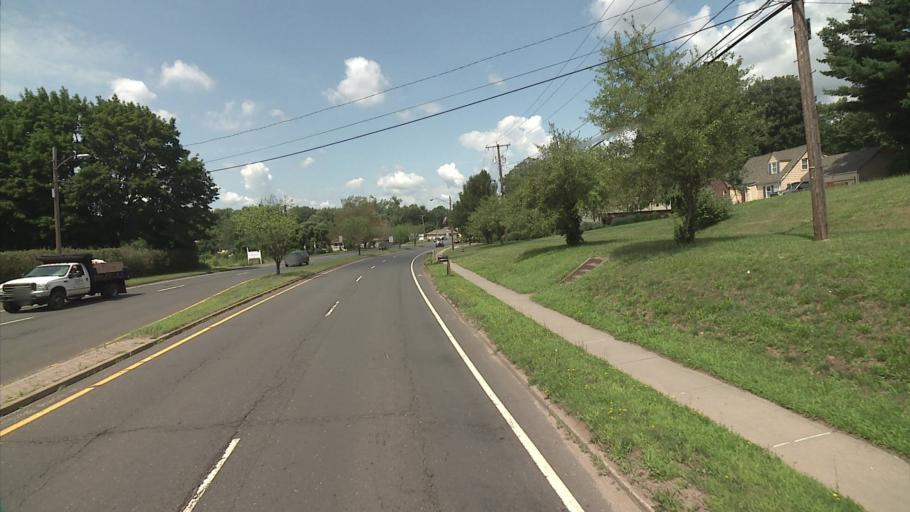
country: US
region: Connecticut
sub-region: Middlesex County
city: Portland
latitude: 41.5687
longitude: -72.6286
